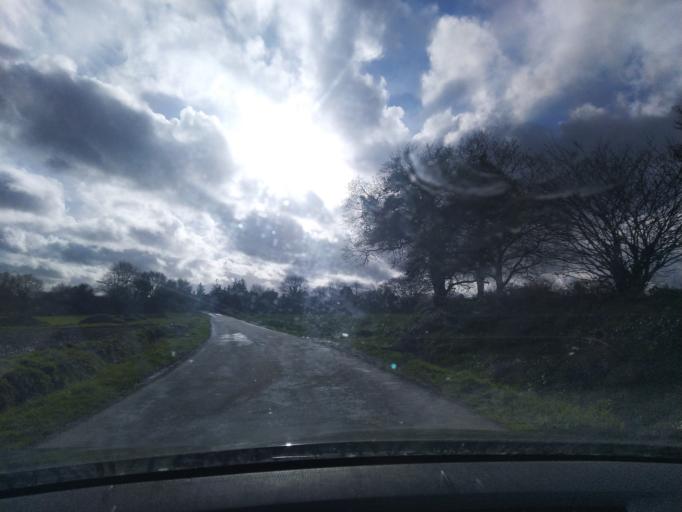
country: FR
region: Brittany
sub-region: Departement du Finistere
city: Guerlesquin
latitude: 48.4492
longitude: -3.5853
